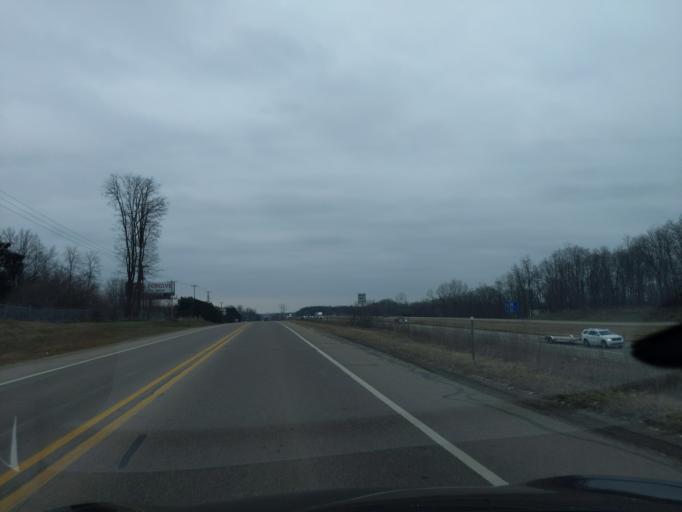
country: US
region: Michigan
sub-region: Eaton County
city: Potterville
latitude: 42.6423
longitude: -84.7081
